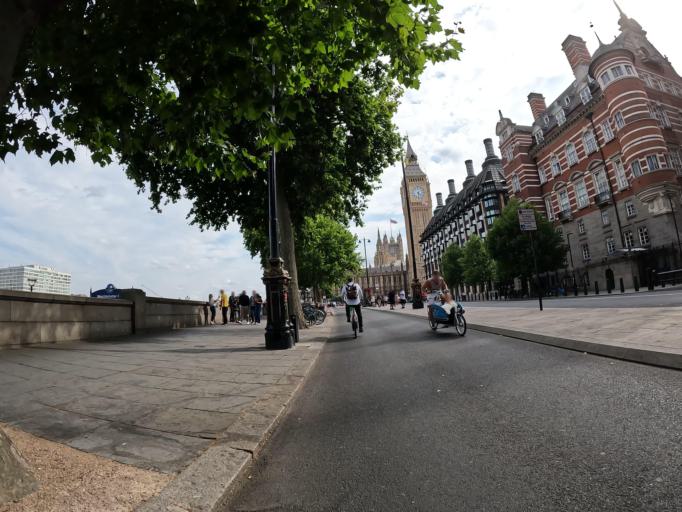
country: GB
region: England
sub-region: Greater London
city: Orpington
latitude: 51.3653
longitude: 0.0522
